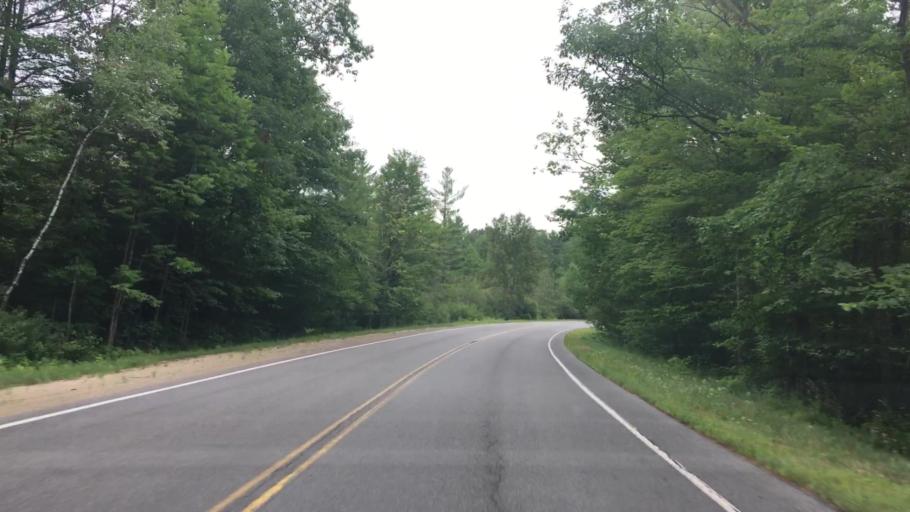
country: US
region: New York
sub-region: Essex County
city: Keeseville
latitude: 44.4786
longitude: -73.5964
